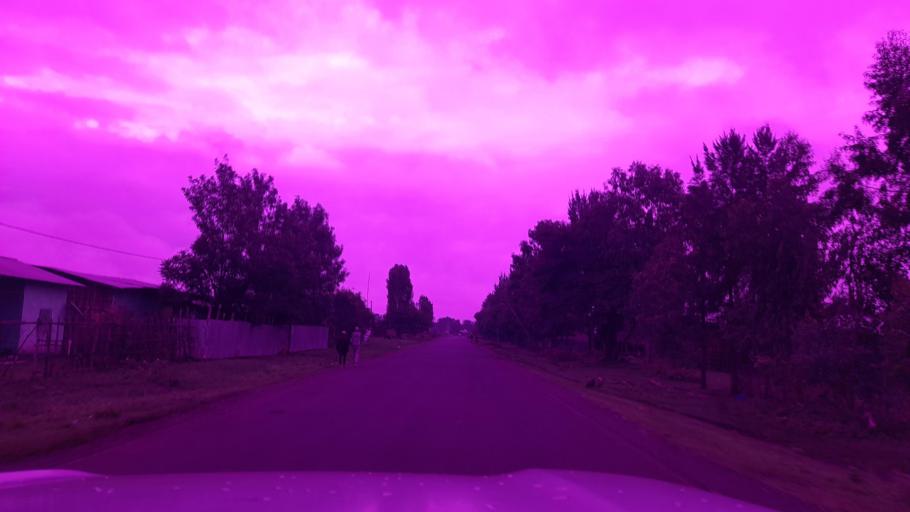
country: ET
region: Oromiya
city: Waliso
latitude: 8.2698
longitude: 37.6599
